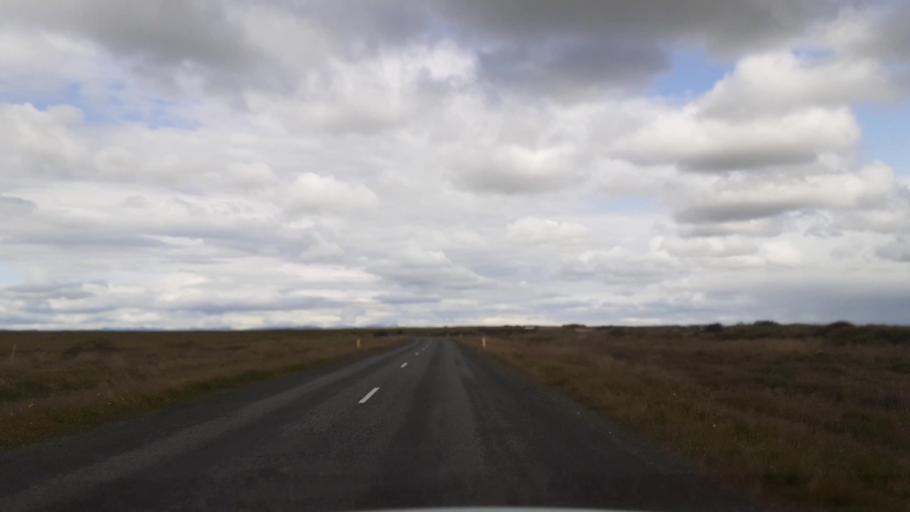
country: IS
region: South
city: Vestmannaeyjar
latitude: 63.8211
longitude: -20.4274
